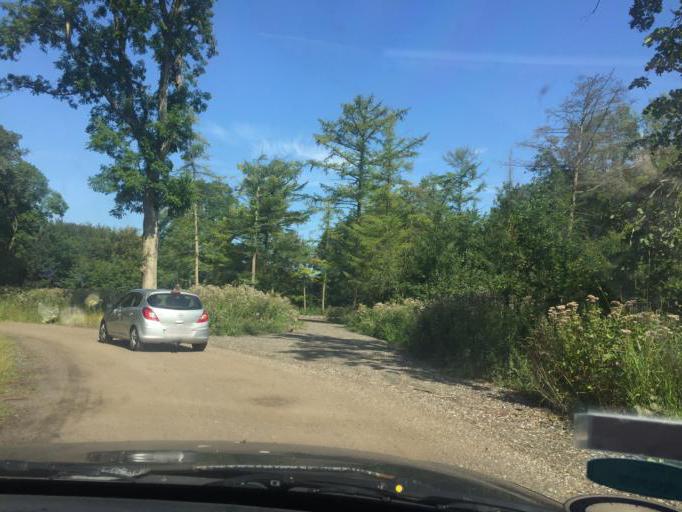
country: DK
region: Zealand
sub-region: Lolland Kommune
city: Maribo
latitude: 54.8148
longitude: 11.5054
